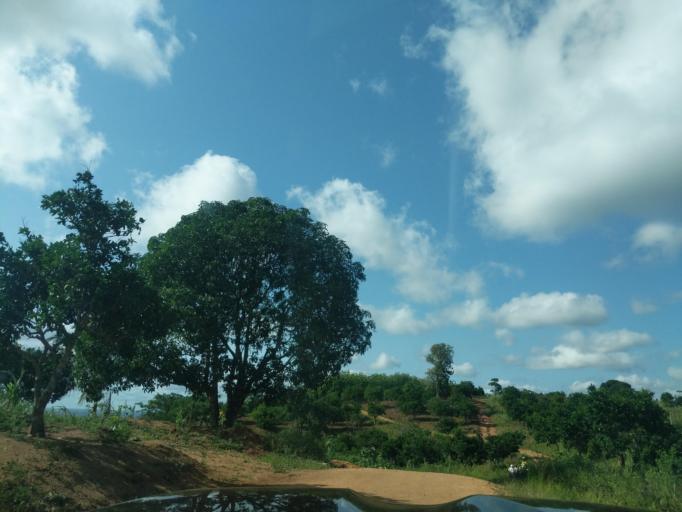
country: TZ
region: Tanga
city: Muheza
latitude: -5.4225
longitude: 38.6360
